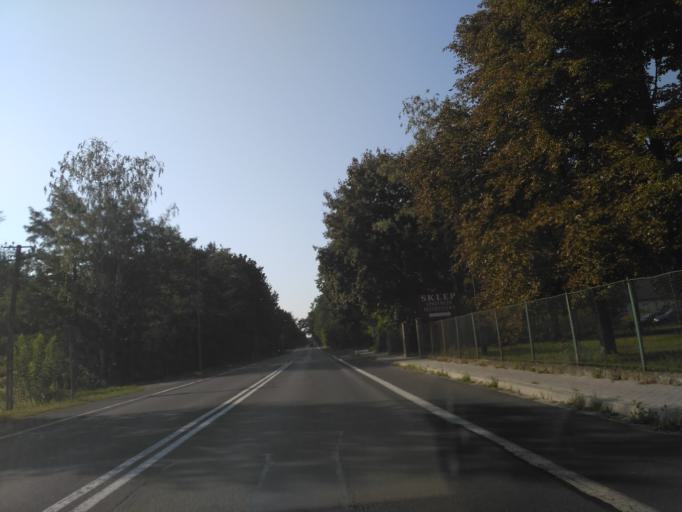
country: PL
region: Subcarpathian Voivodeship
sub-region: Powiat rzeszowski
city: Gorno
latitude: 50.2849
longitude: 22.1351
